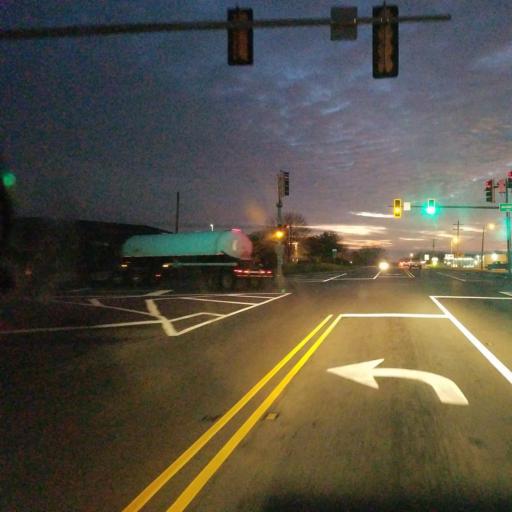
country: US
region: Illinois
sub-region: Peoria County
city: Bellevue
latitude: 40.6886
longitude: -89.6939
